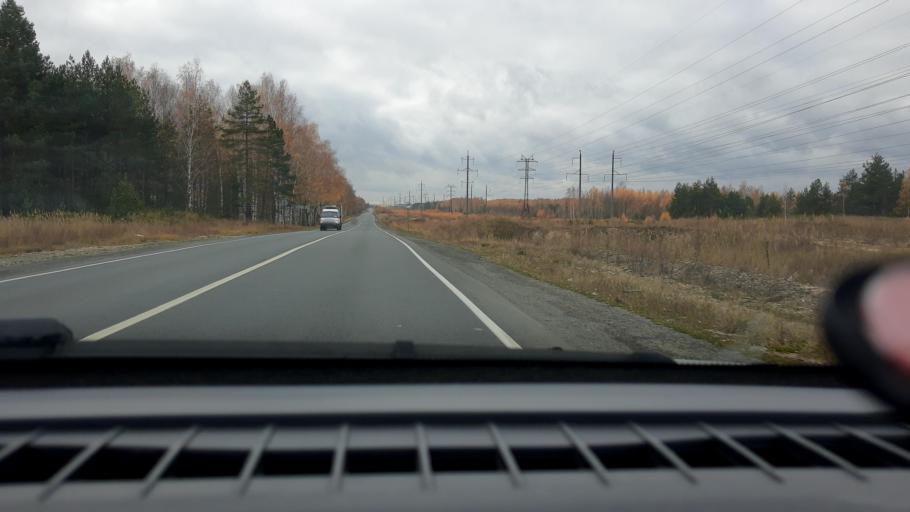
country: RU
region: Nizjnij Novgorod
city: Lukino
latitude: 56.3589
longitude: 43.5935
